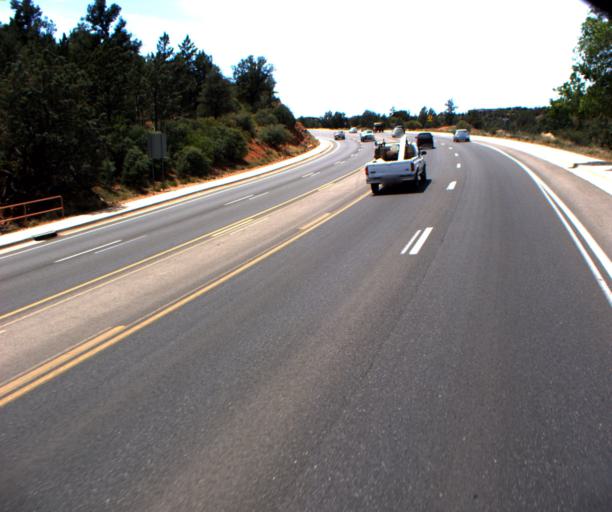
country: US
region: Arizona
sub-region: Coconino County
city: Sedona
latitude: 34.8675
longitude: -111.7698
